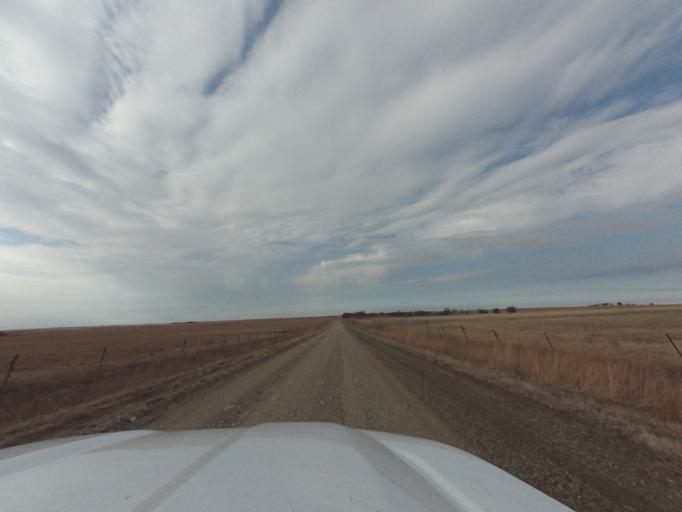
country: US
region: Kansas
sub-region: Chase County
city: Cottonwood Falls
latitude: 38.2171
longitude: -96.7027
